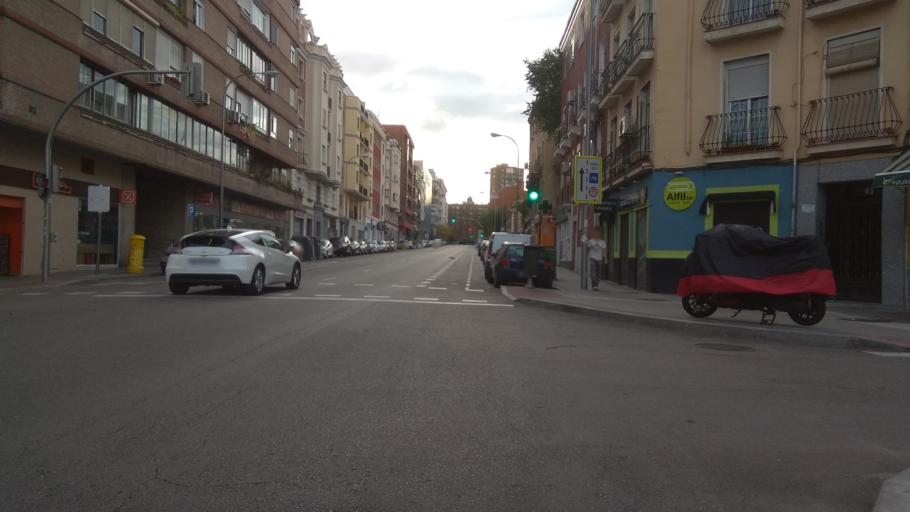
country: ES
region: Madrid
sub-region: Provincia de Madrid
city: Salamanca
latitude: 40.4324
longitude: -3.6671
